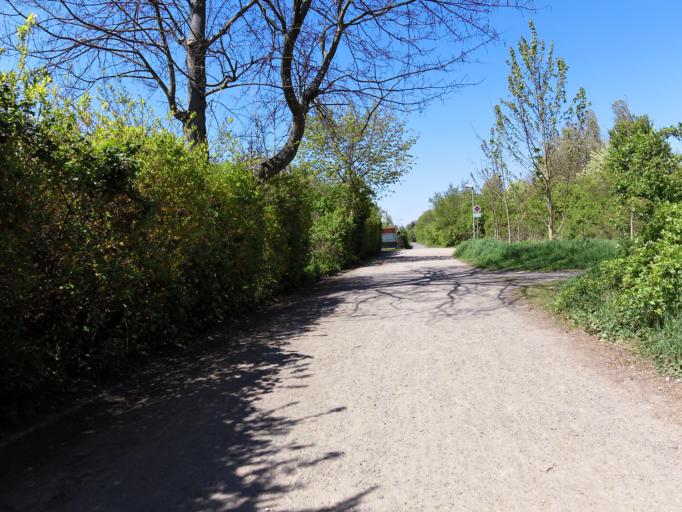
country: DE
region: Saxony
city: Leipzig
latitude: 51.3611
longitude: 12.3489
